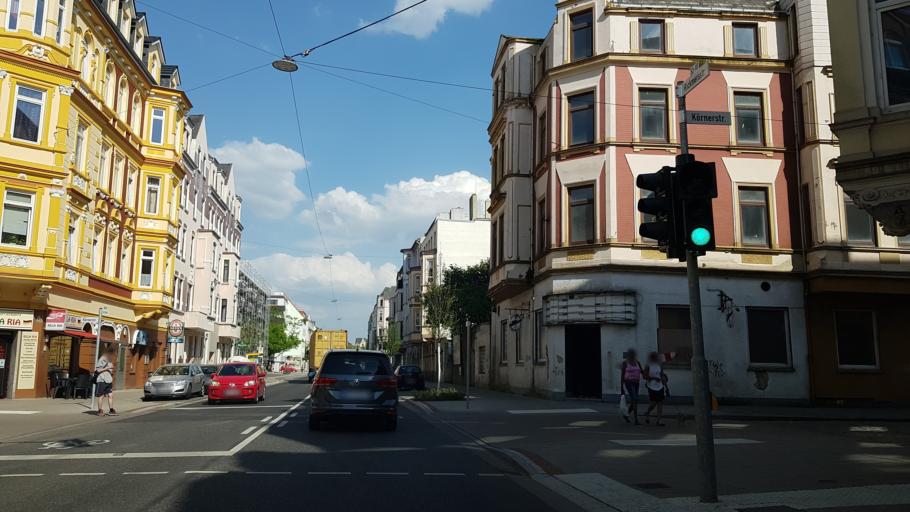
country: DE
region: Bremen
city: Bremerhaven
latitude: 53.5606
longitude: 8.5782
